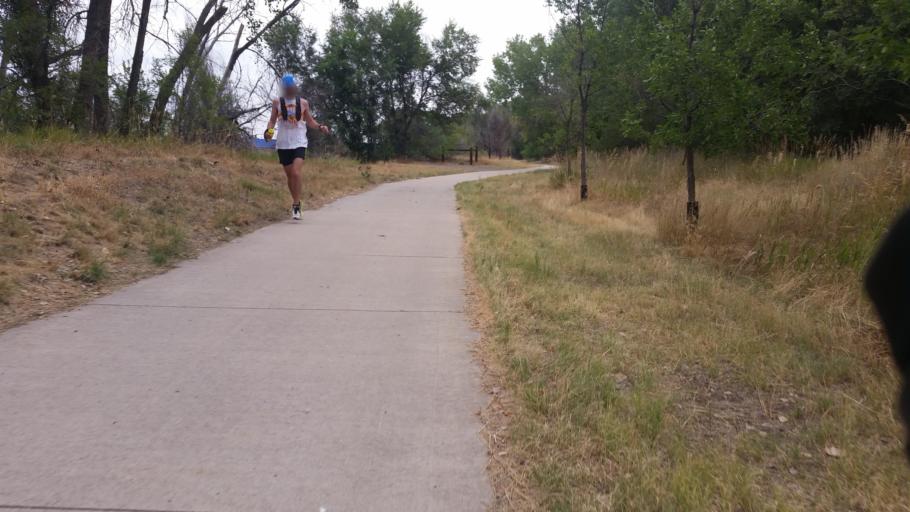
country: US
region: Colorado
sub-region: Adams County
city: Welby
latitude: 39.8260
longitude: -104.9666
